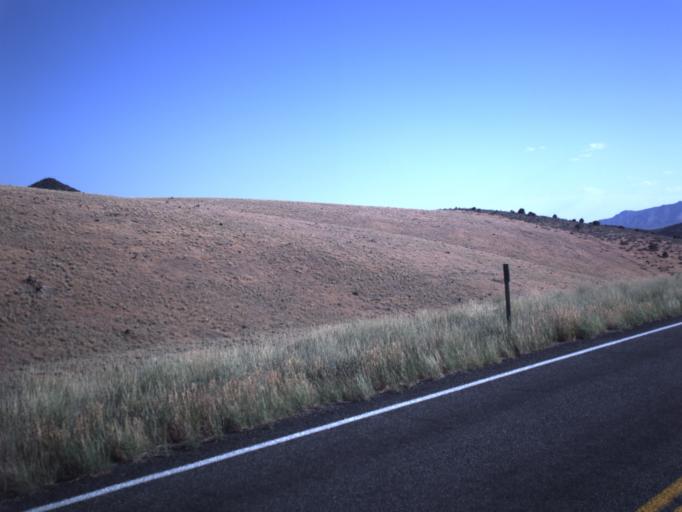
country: US
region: Utah
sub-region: Iron County
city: Parowan
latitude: 38.0874
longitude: -112.9543
